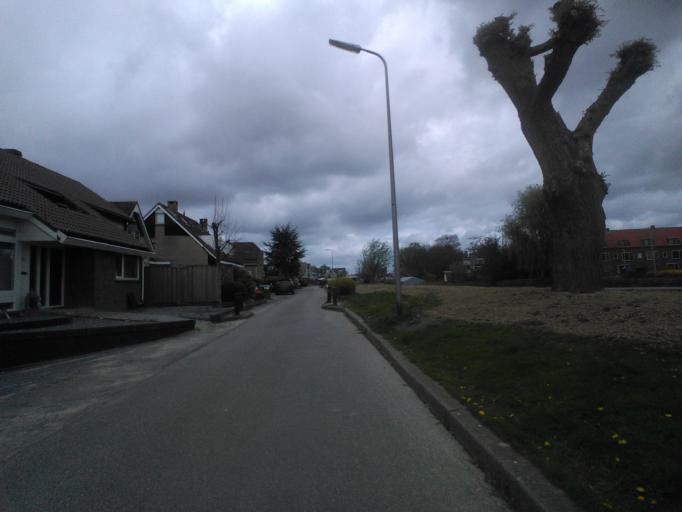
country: NL
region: South Holland
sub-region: Gemeente Gouda
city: Bloemendaal
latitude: 51.9858
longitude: 4.6657
